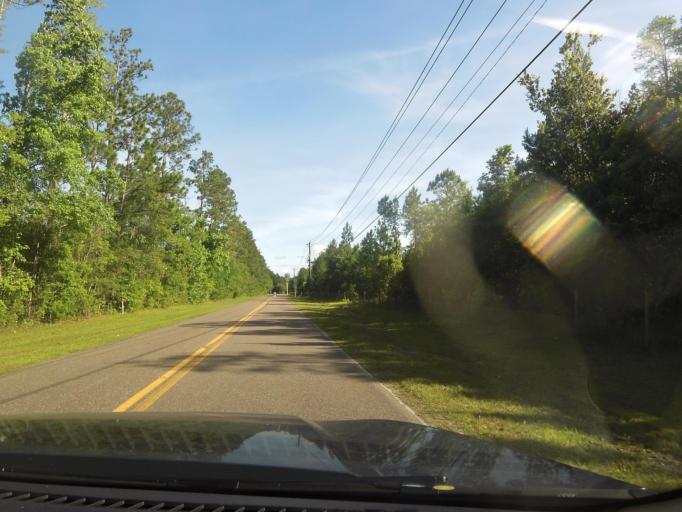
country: US
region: Florida
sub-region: Nassau County
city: Callahan
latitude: 30.5541
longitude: -81.7928
